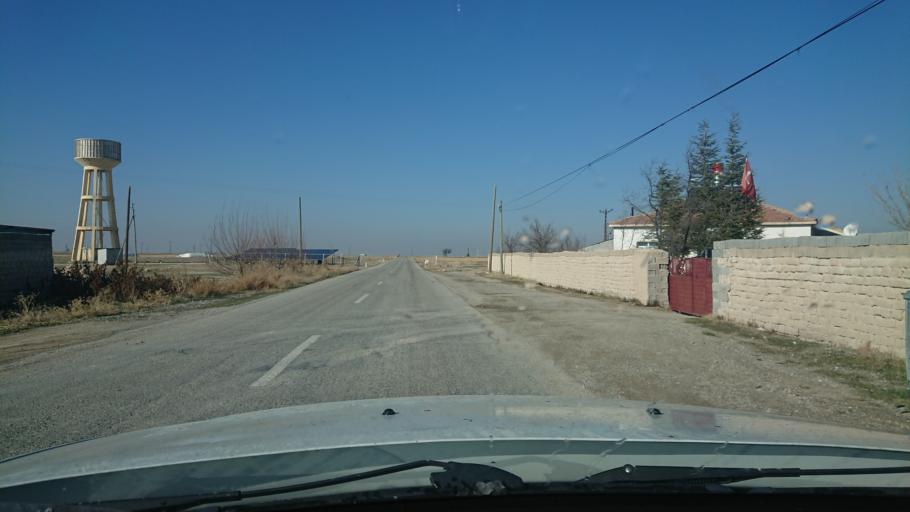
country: TR
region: Aksaray
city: Sultanhani
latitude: 38.2942
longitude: 33.5163
